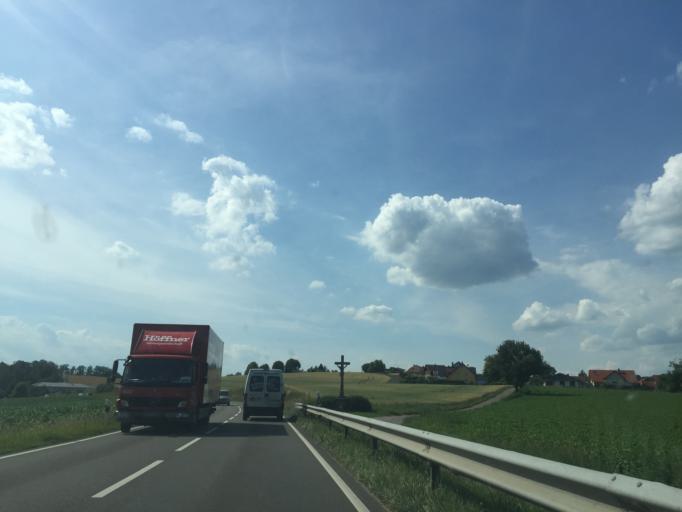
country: DE
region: Baden-Wuerttemberg
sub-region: Karlsruhe Region
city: Horrenberg
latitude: 49.2870
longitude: 8.7739
